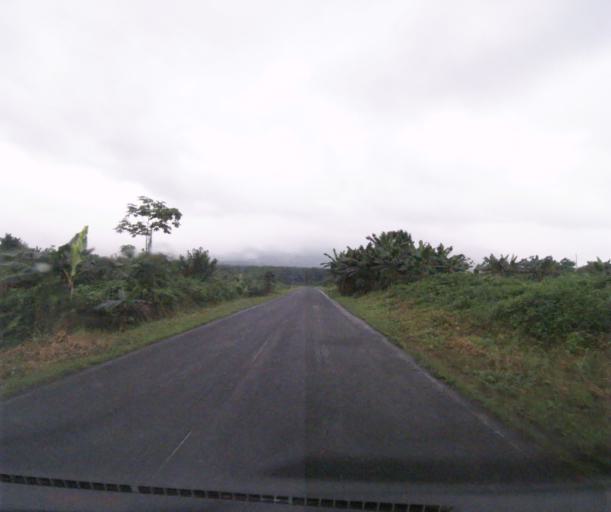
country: CM
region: South-West Province
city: Idenao
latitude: 4.2028
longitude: 8.9990
